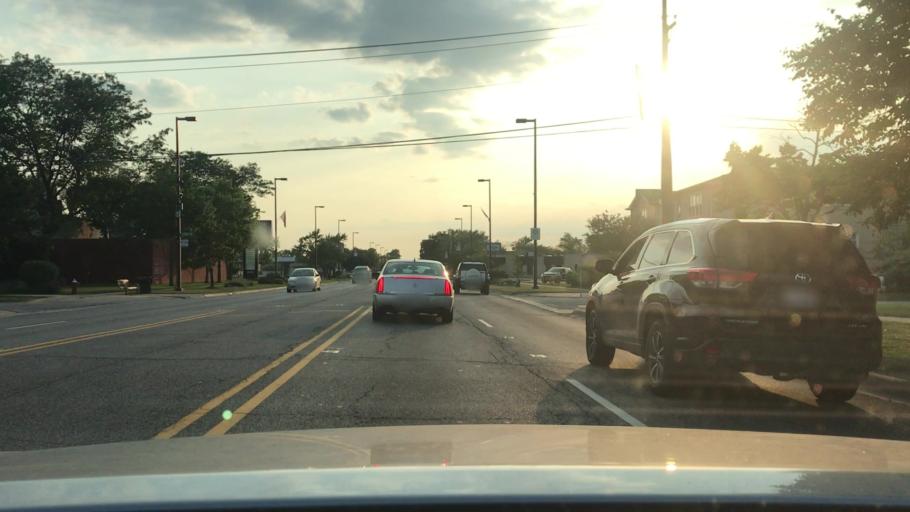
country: US
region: Illinois
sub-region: Cook County
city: Hometown
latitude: 41.7491
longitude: -87.7433
